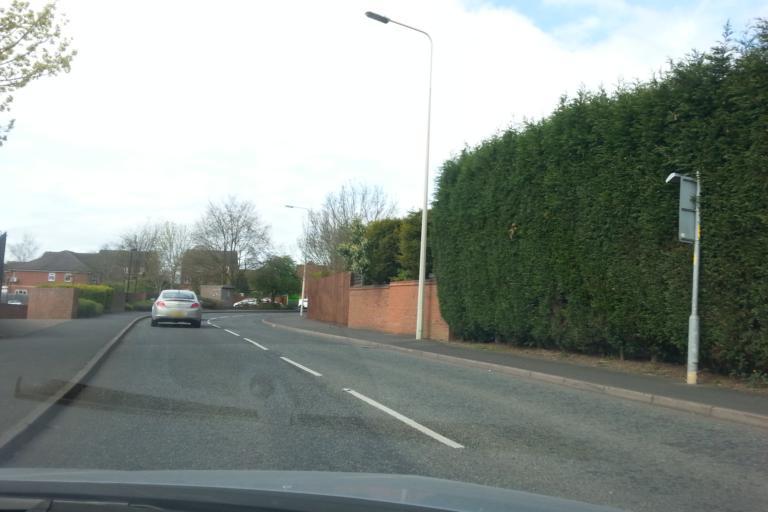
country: GB
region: England
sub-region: Dudley
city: Dudley
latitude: 52.5184
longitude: -2.1132
